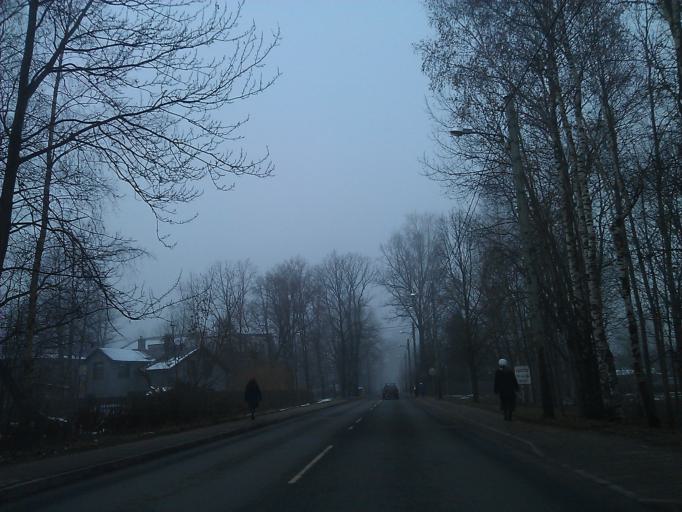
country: LV
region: Riga
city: Riga
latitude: 56.9083
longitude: 24.0936
